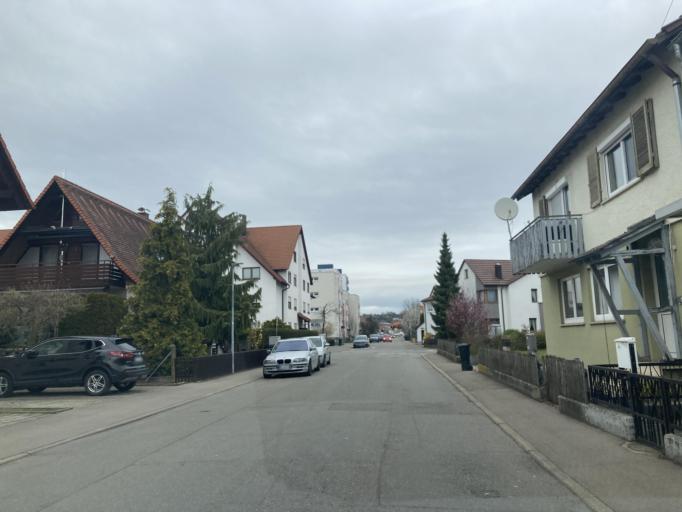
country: DE
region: Baden-Wuerttemberg
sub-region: Tuebingen Region
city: Rottenburg
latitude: 48.4772
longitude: 8.9464
